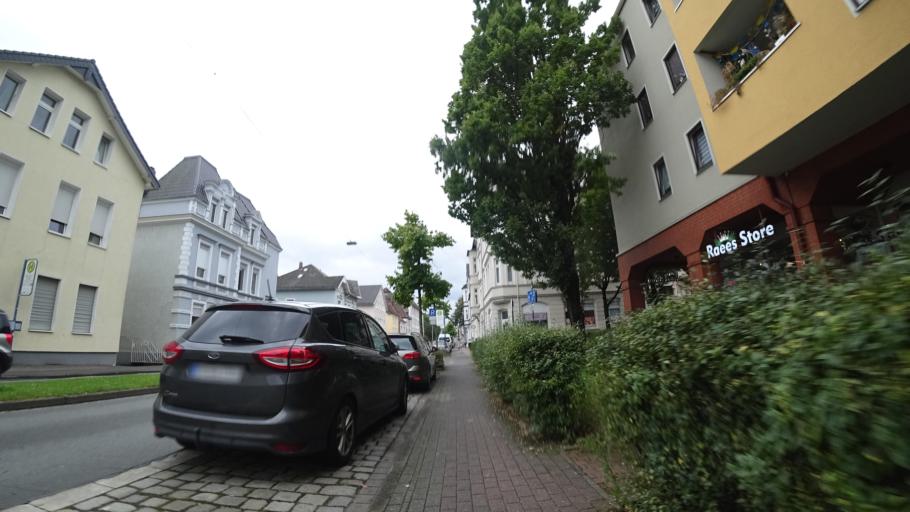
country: DE
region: North Rhine-Westphalia
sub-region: Regierungsbezirk Detmold
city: Bielefeld
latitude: 52.0292
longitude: 8.5397
